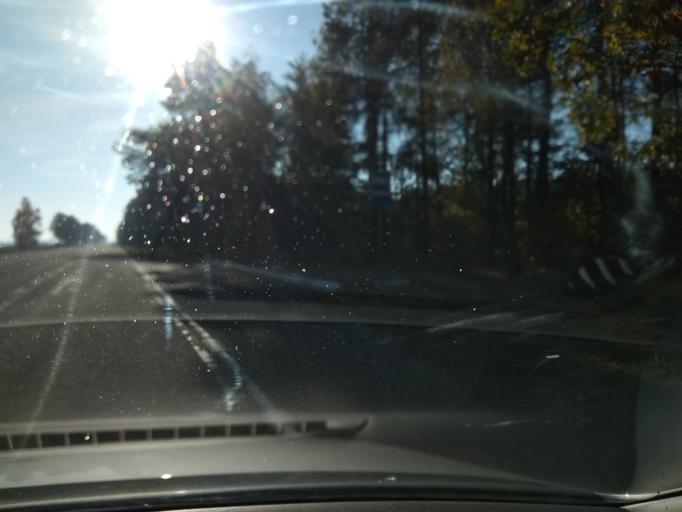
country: BY
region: Brest
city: Malaryta
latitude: 51.8714
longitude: 24.1811
